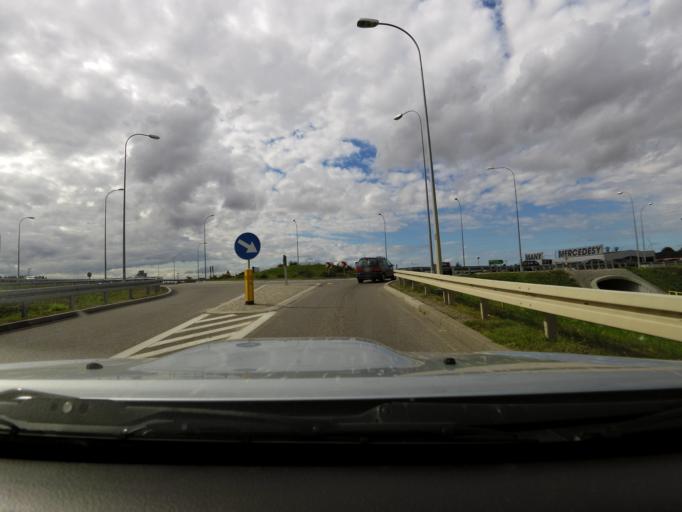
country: PL
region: Pomeranian Voivodeship
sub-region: Powiat nowodworski
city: Nowy Dwor Gdanski
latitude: 54.2135
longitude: 19.1056
